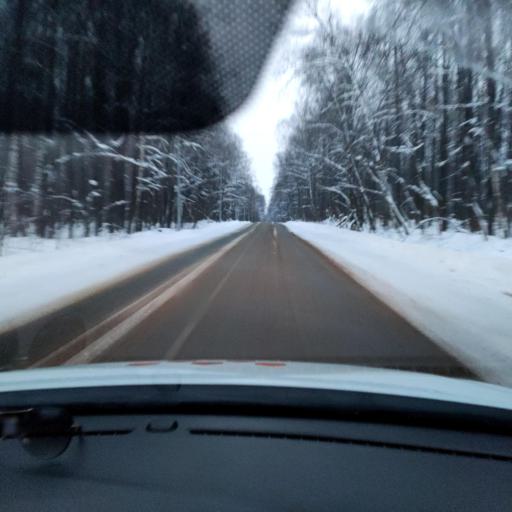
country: RU
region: Tatarstan
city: Vysokaya Gora
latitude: 55.9353
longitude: 49.1750
